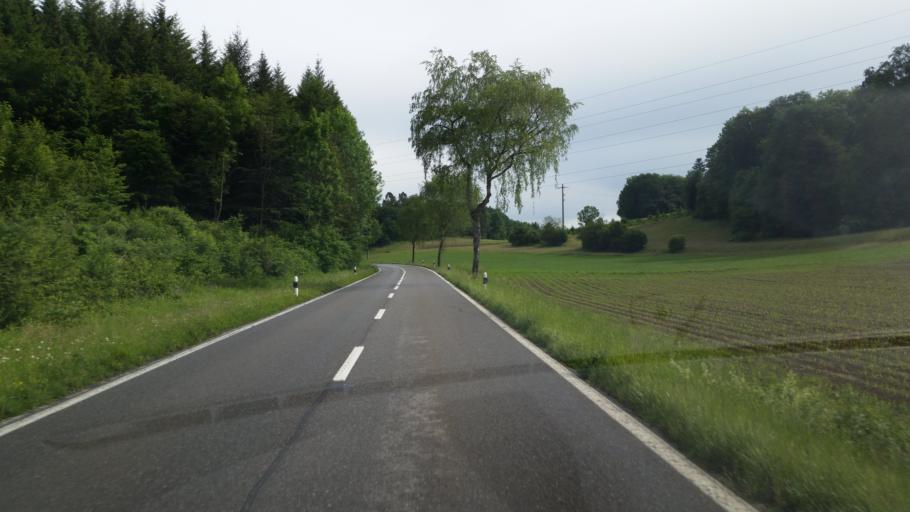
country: CH
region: Aargau
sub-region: Bezirk Muri
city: Aristau
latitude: 47.3128
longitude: 8.3542
